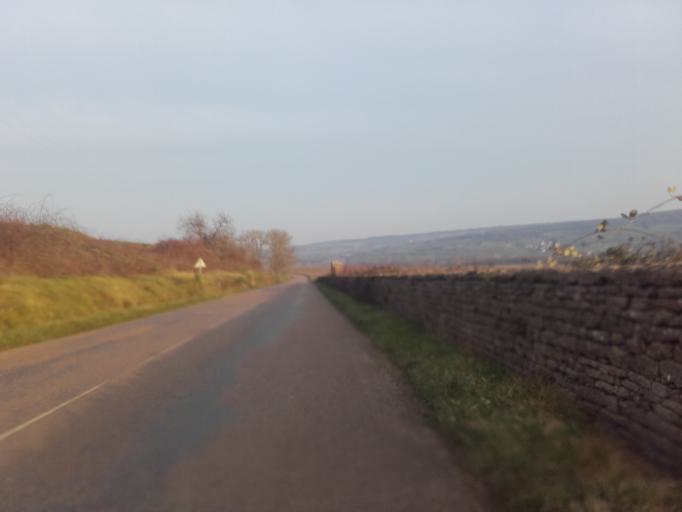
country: FR
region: Bourgogne
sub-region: Departement de la Cote-d'Or
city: Nolay
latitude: 46.9090
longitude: 4.6645
